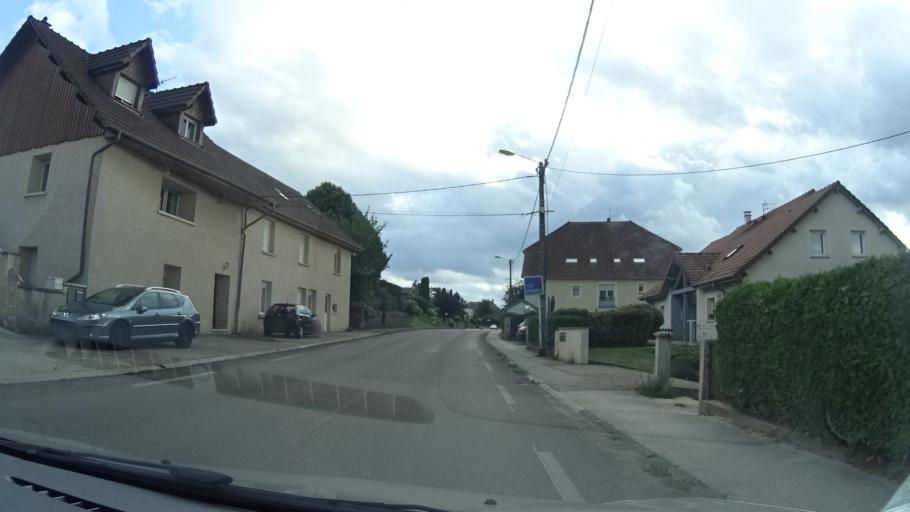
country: FR
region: Franche-Comte
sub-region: Departement du Doubs
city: Saone
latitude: 47.2229
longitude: 6.1152
